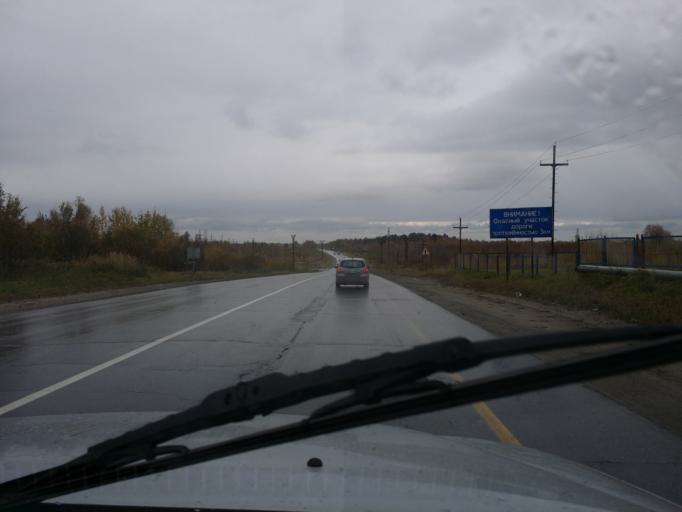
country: RU
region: Khanty-Mansiyskiy Avtonomnyy Okrug
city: Megion
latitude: 61.0554
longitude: 76.1137
